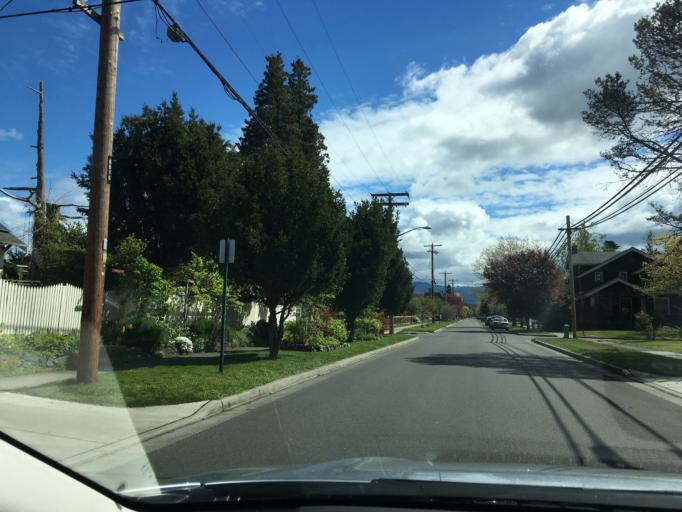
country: US
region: Washington
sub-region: Whatcom County
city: Bellingham
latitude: 48.7619
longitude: -122.4960
